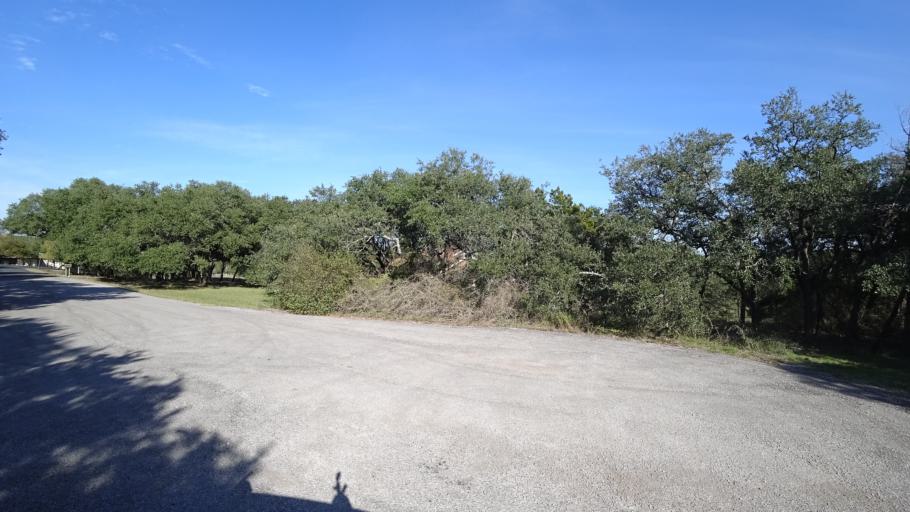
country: US
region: Texas
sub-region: Travis County
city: Bee Cave
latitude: 30.2342
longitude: -97.9371
